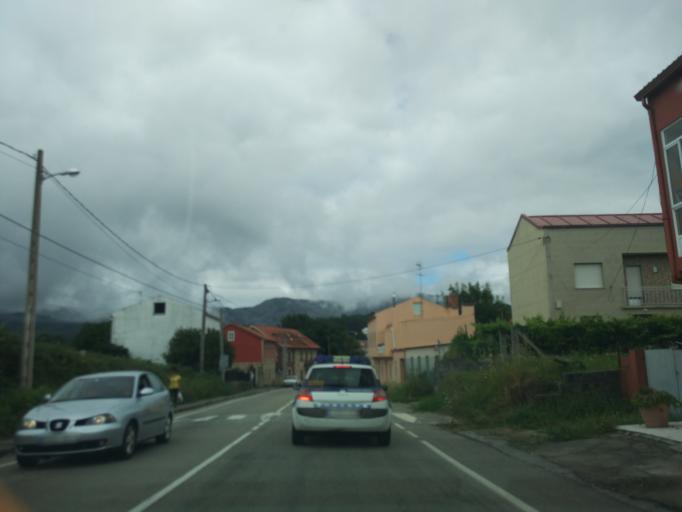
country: ES
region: Galicia
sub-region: Provincia da Coruna
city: Boiro
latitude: 42.6458
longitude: -8.8743
